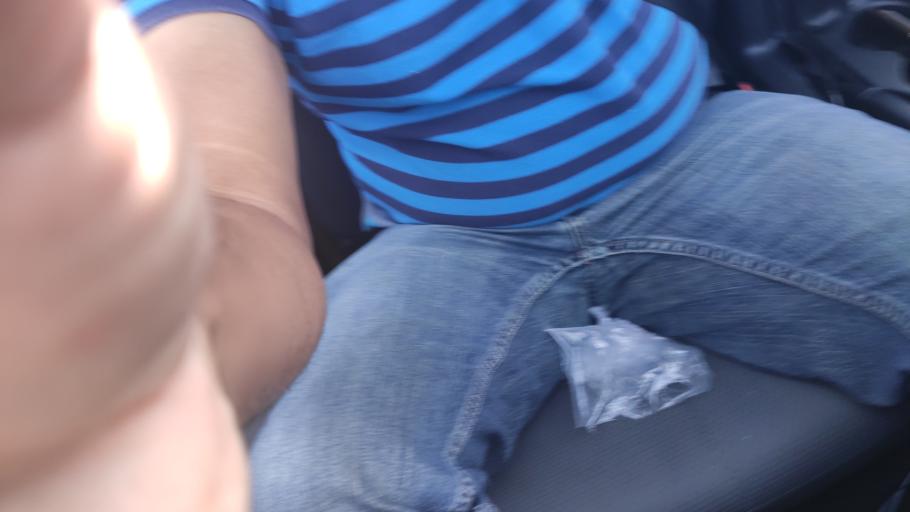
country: CV
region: Mosteiros
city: Porto dos Mosteiros
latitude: 15.0201
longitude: -24.3951
